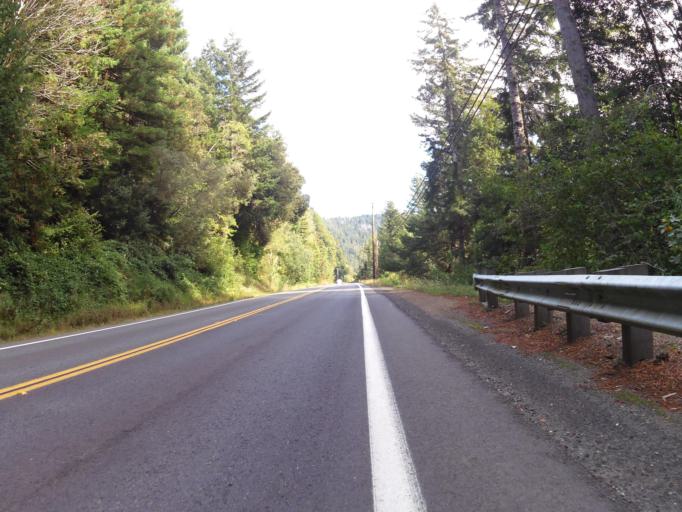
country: US
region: California
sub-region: Del Norte County
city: Bertsch-Oceanview
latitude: 41.8162
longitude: -124.0904
